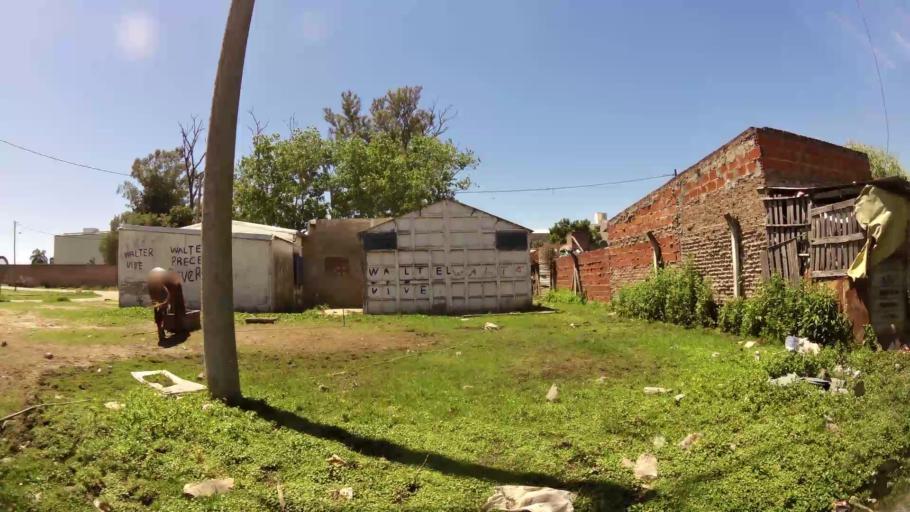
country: AR
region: Santa Fe
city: Santa Fe de la Vera Cruz
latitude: -31.6151
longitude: -60.7209
